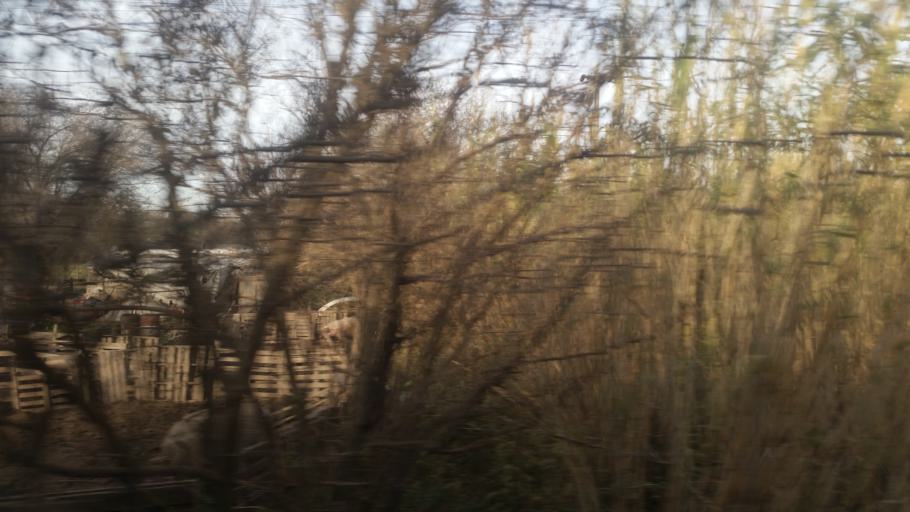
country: AR
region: Cordoba
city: Leones
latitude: -32.6312
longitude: -62.4872
